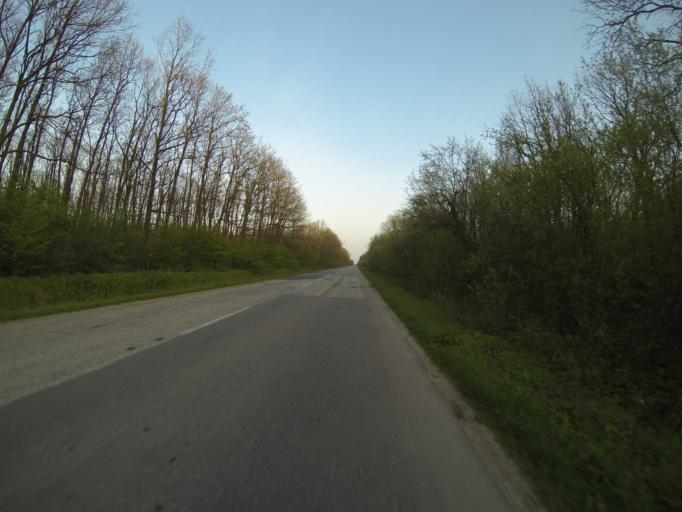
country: RO
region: Dolj
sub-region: Comuna Dranicu
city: Dranic
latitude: 44.0663
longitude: 23.8078
